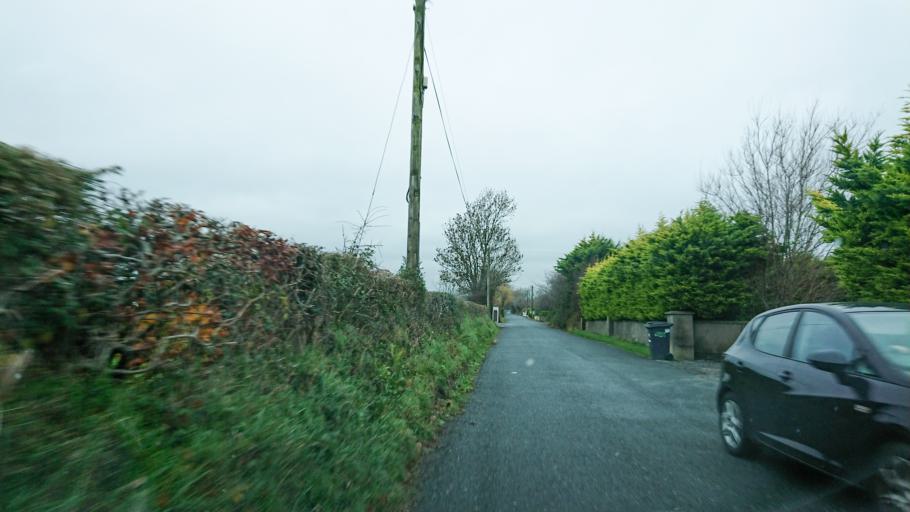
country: IE
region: Munster
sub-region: Waterford
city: Waterford
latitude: 52.2387
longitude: -7.1793
